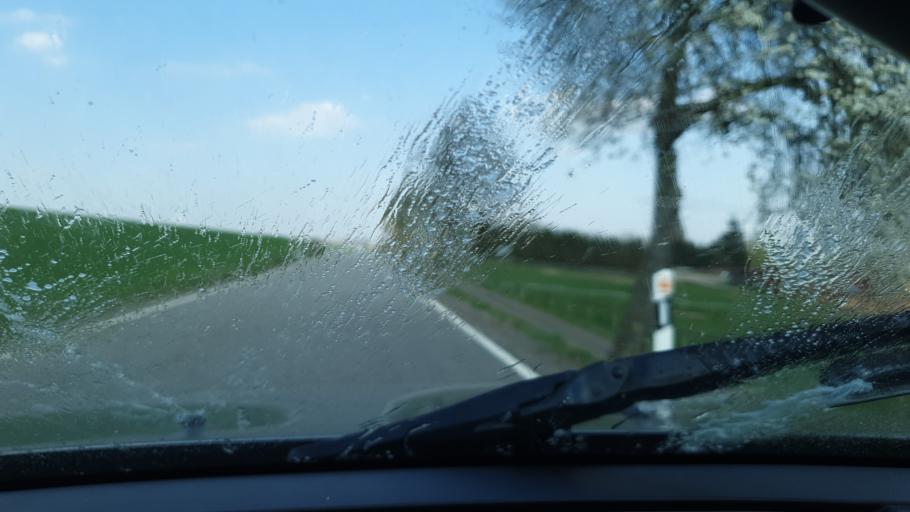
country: DE
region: Rheinland-Pfalz
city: Knopp-Labach
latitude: 49.3304
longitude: 7.4961
